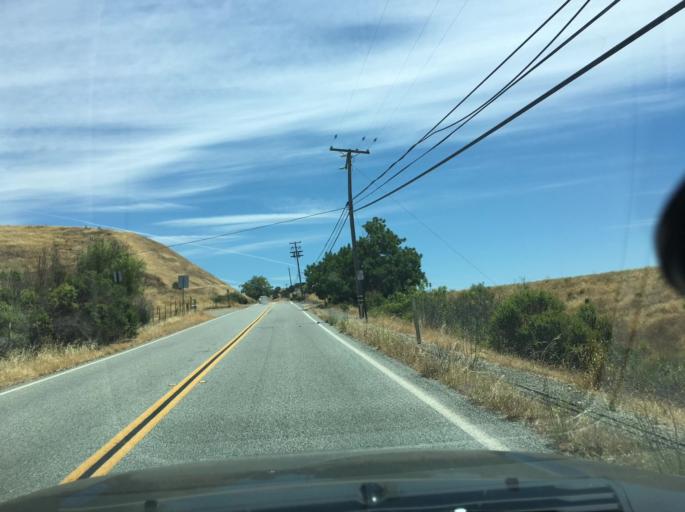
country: US
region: California
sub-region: Santa Clara County
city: Seven Trees
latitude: 37.1882
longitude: -121.7813
